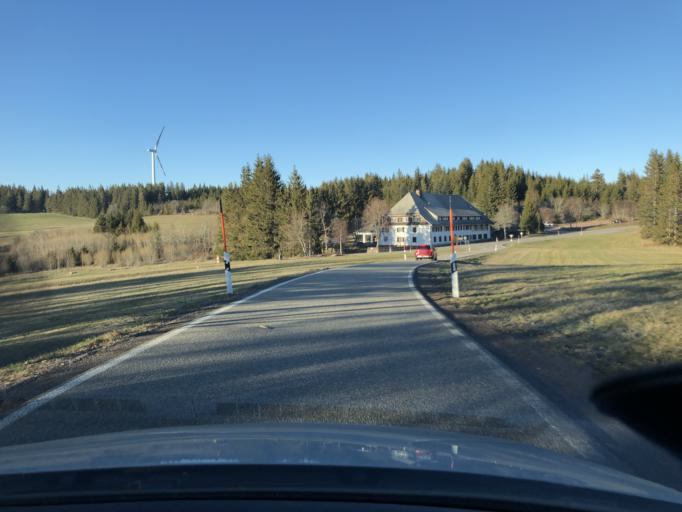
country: DE
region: Baden-Wuerttemberg
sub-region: Freiburg Region
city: Schluchsee
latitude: 47.8285
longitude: 8.2088
